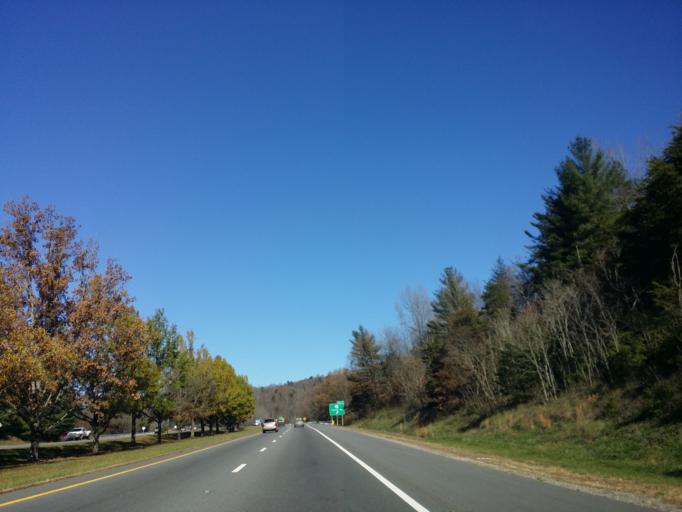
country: US
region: North Carolina
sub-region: Buncombe County
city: Asheville
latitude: 35.5803
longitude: -82.5197
